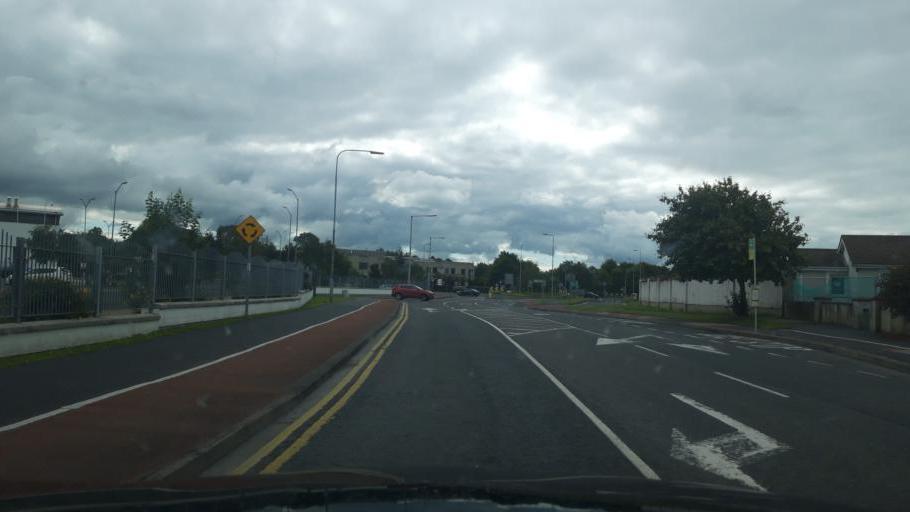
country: IE
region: Leinster
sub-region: Kilkenny
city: Kilkenny
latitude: 52.6387
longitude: -7.2384
